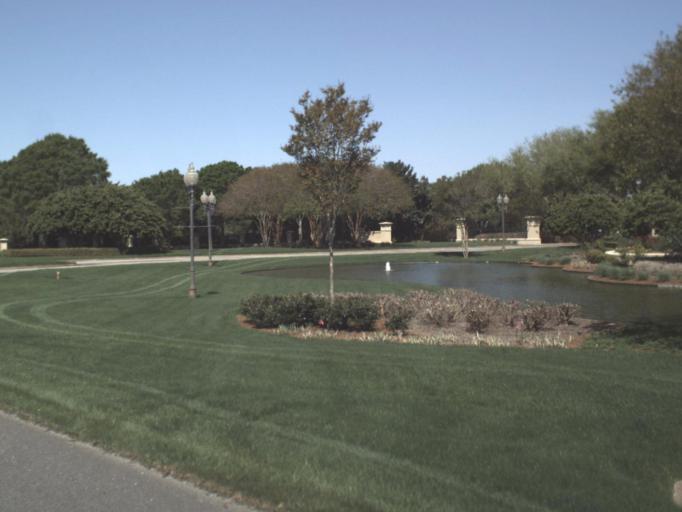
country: US
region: Florida
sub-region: Okaloosa County
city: Destin
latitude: 30.3877
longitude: -86.4343
